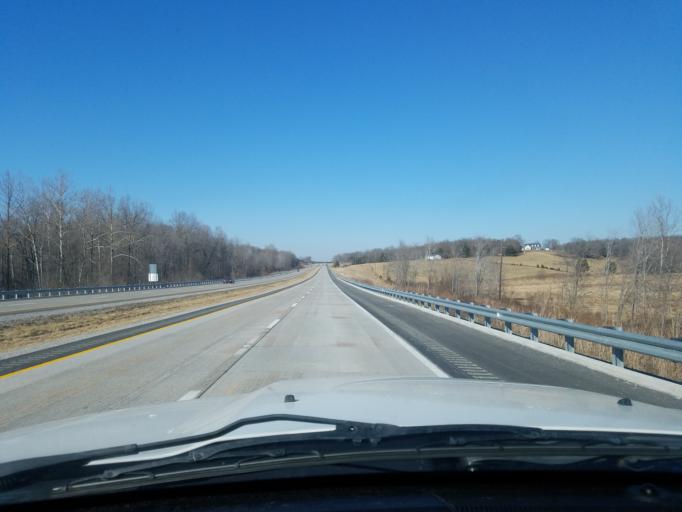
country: US
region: Kentucky
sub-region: Ohio County
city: Beaver Dam
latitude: 37.4017
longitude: -86.8214
